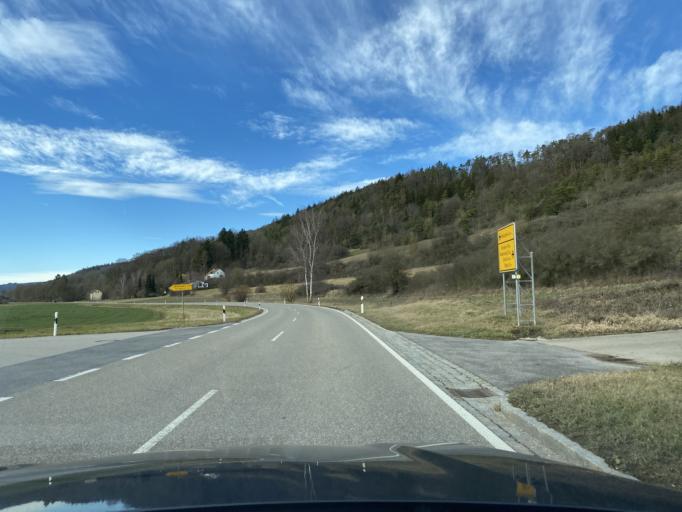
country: DE
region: Bavaria
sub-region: Upper Palatinate
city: Dietfurt
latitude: 49.0219
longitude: 11.5264
